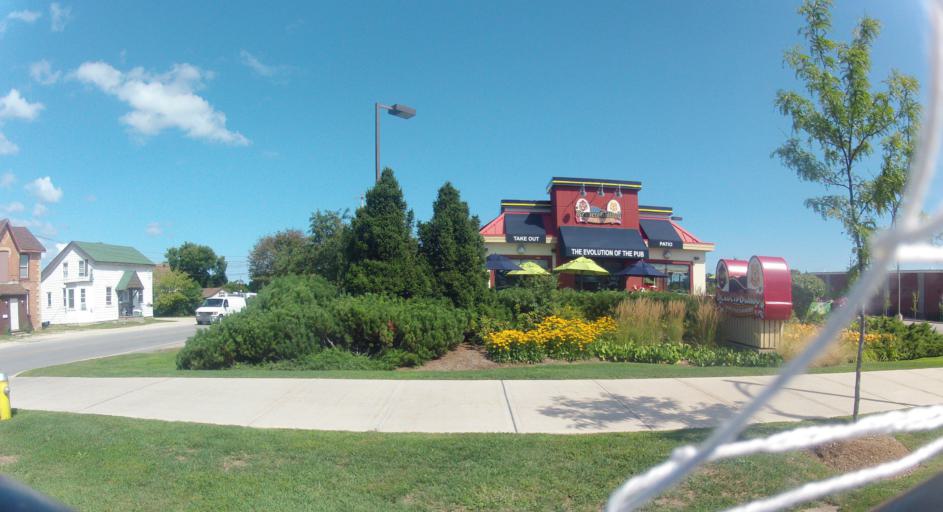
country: CA
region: Ontario
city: Collingwood
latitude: 44.5023
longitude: -80.2235
